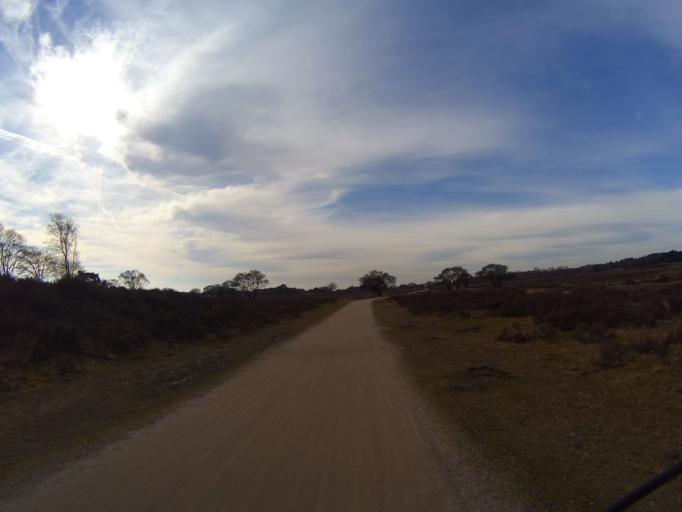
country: NL
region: North Holland
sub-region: Gemeente Laren
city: Laren
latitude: 52.2350
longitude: 5.2180
